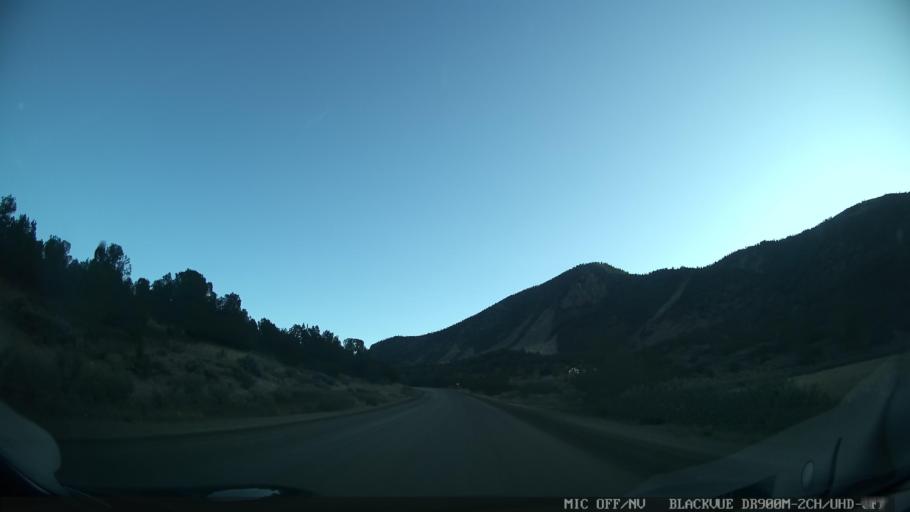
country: US
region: Colorado
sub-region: Grand County
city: Kremmling
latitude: 39.9795
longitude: -106.4981
